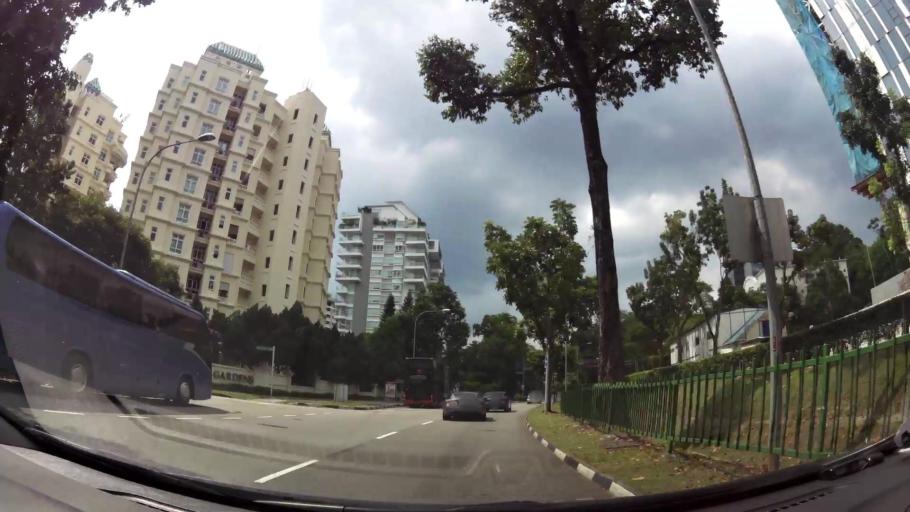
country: SG
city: Singapore
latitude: 1.3135
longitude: 103.8279
